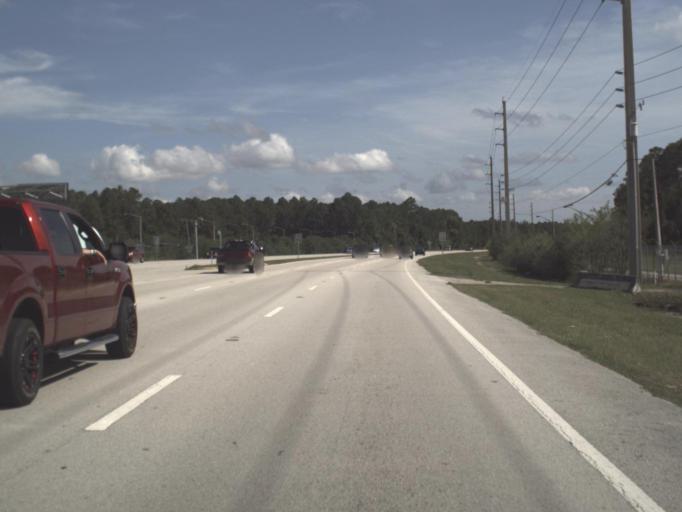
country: US
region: Florida
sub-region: Clay County
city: Orange Park
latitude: 30.1970
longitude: -81.7075
